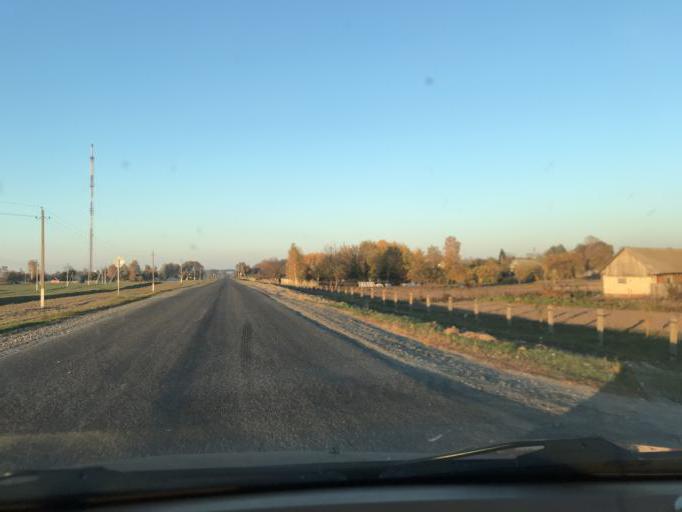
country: BY
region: Gomel
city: Brahin
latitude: 51.7887
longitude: 30.2573
